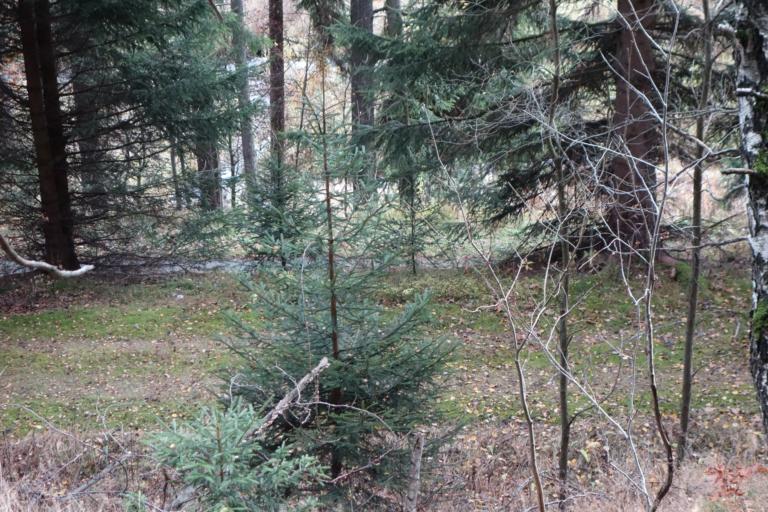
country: DE
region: Saxony
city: Rechenberg-Bienenmuhle
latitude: 50.7250
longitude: 13.6330
